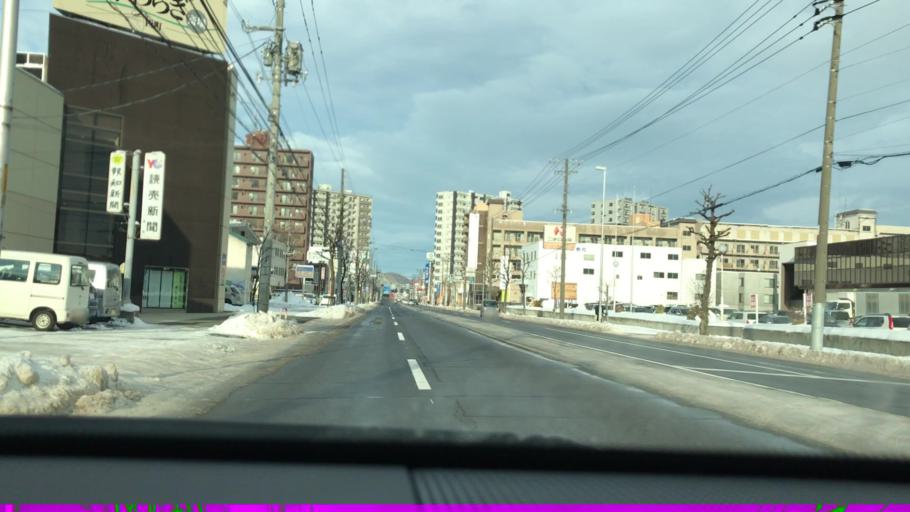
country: JP
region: Hokkaido
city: Sapporo
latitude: 43.0851
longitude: 141.2785
